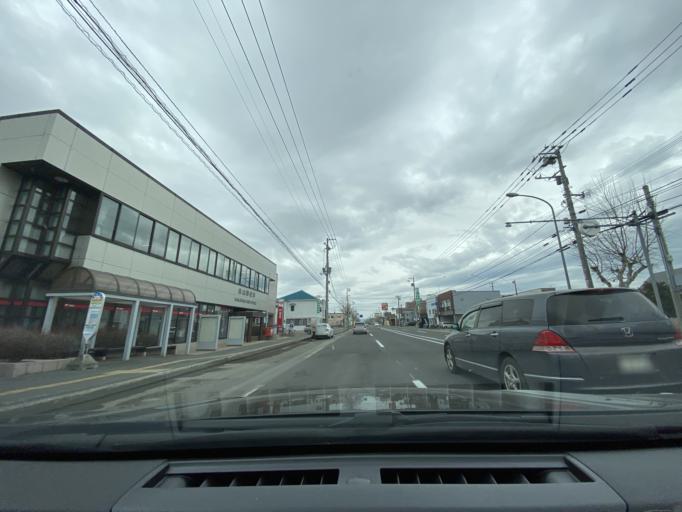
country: JP
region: Hokkaido
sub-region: Asahikawa-shi
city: Asahikawa
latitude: 43.8101
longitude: 142.4331
